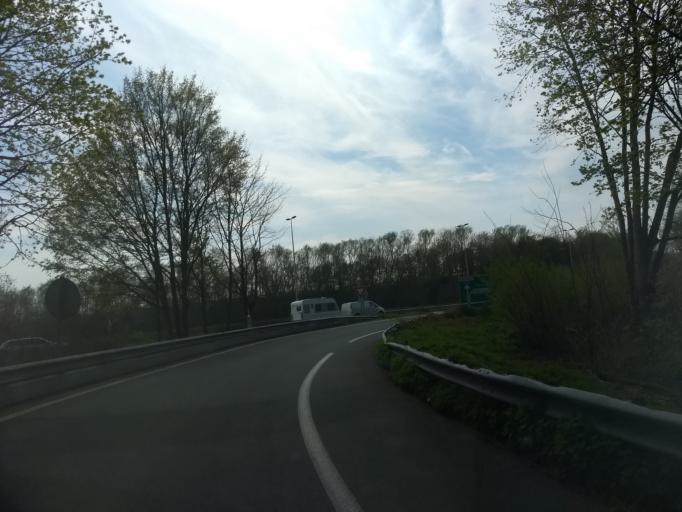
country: FR
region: Nord-Pas-de-Calais
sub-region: Departement du Nord
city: Lambres-lez-Douai
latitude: 50.3573
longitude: 3.0496
